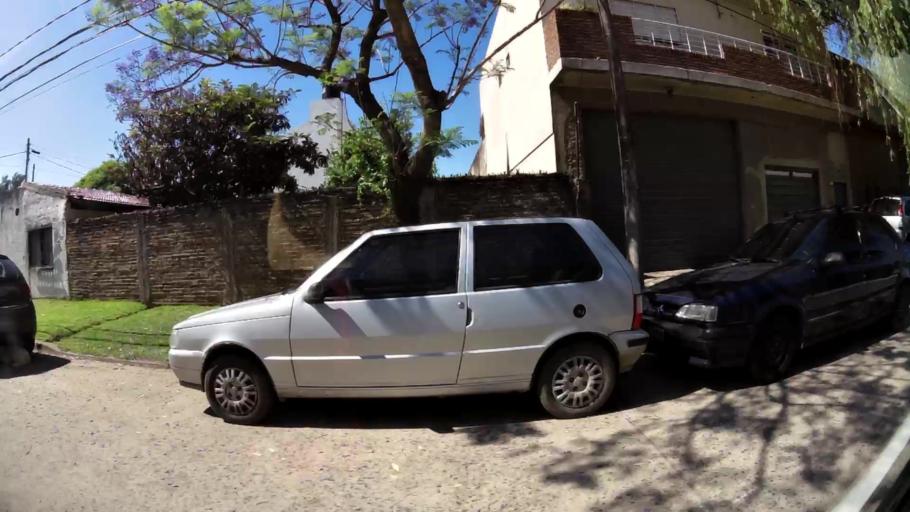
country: AR
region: Buenos Aires
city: Ituzaingo
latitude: -34.6336
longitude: -58.6590
